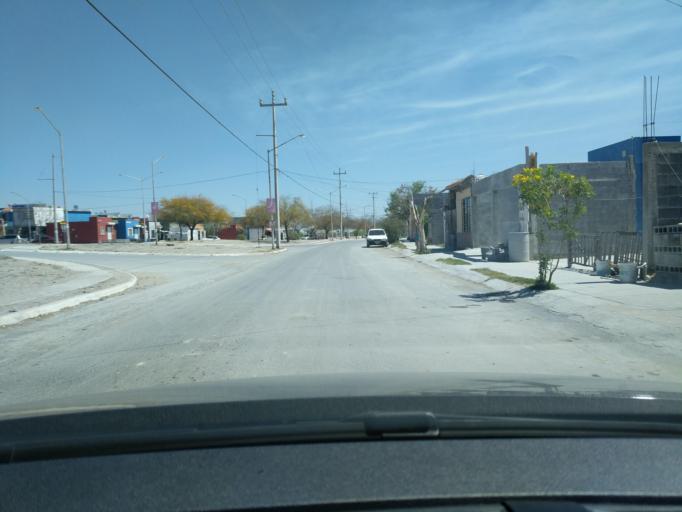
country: MX
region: Nuevo Leon
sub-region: Salinas Victoria
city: Las Torres
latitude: 25.9648
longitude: -100.3071
